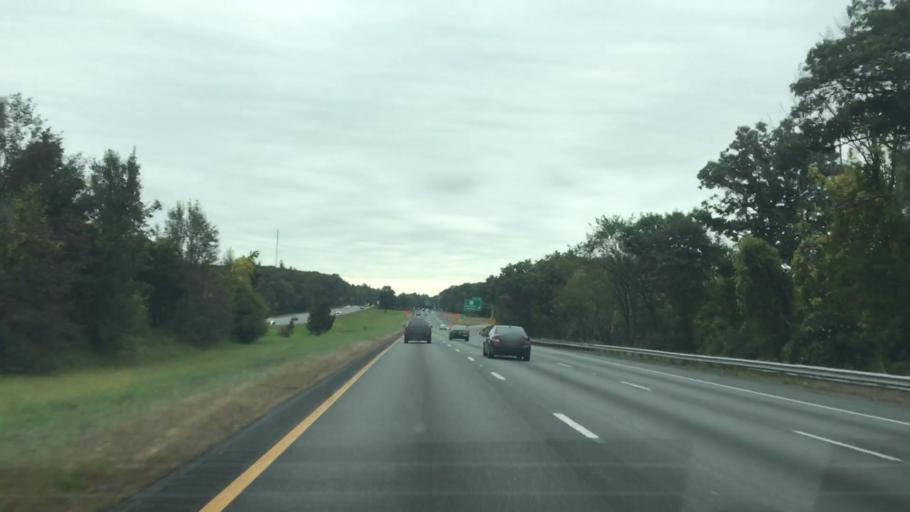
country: US
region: Massachusetts
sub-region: Middlesex County
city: Tewksbury
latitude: 42.6392
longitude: -71.2385
